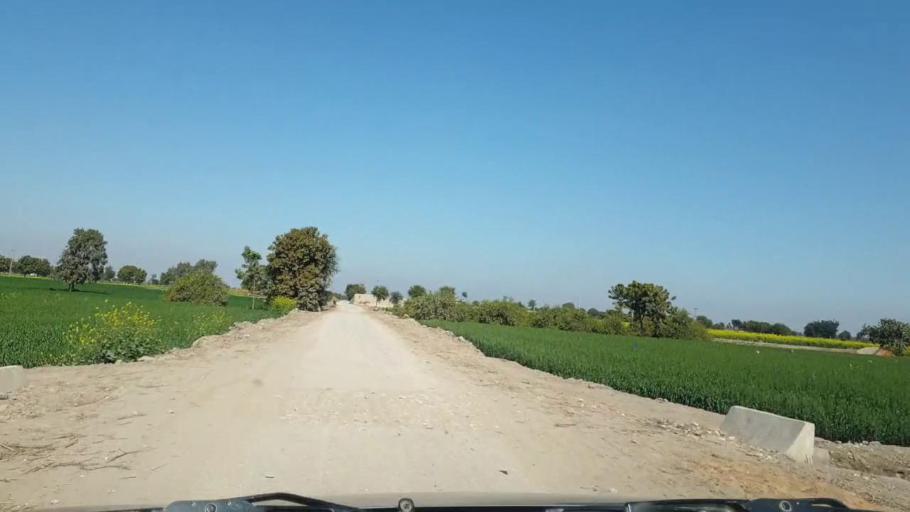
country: PK
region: Sindh
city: Khadro
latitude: 26.1394
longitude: 68.8159
